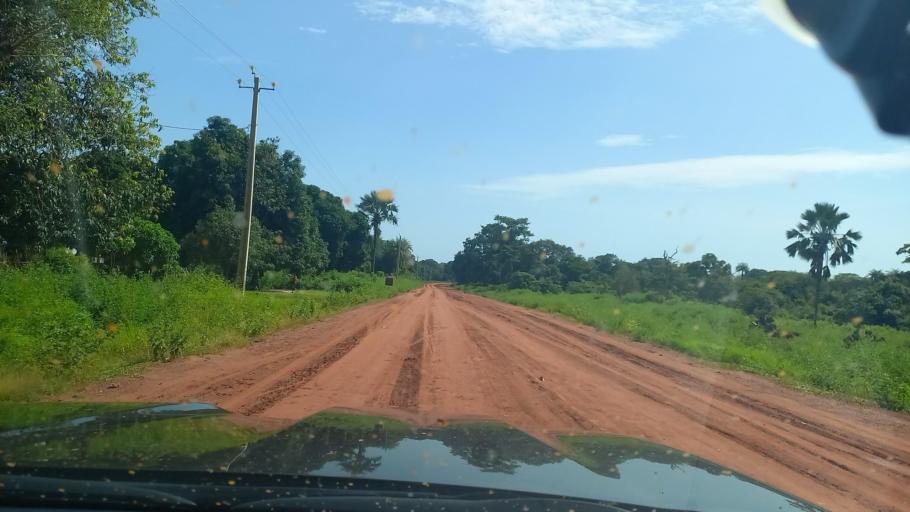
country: SN
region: Ziguinchor
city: Adeane
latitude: 12.6649
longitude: -16.1049
